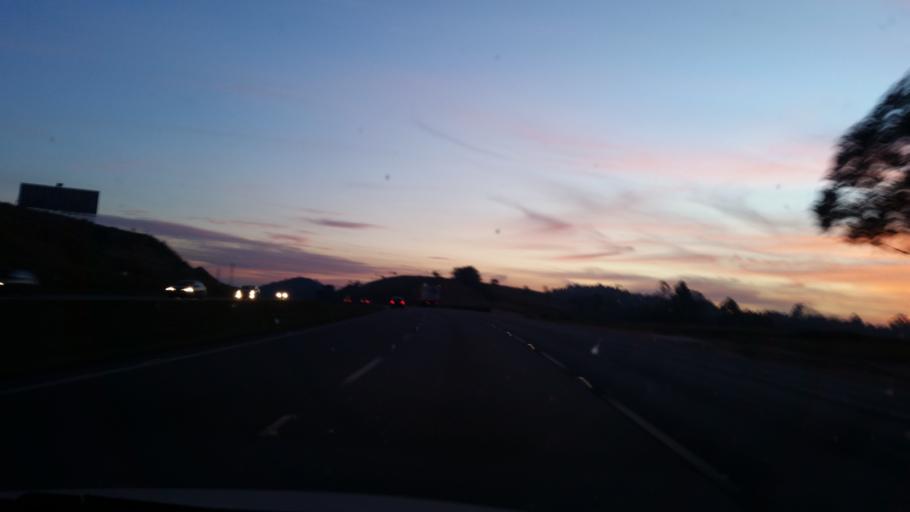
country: BR
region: Sao Paulo
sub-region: Guararema
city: Guararema
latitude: -23.3433
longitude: -46.0379
